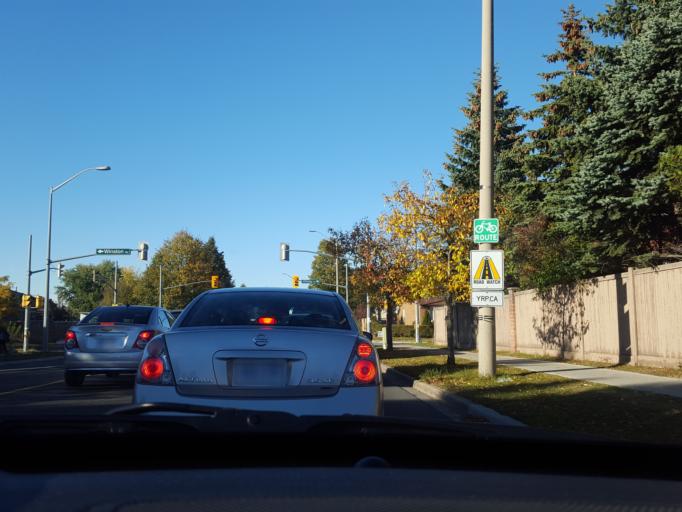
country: CA
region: Ontario
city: Markham
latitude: 43.8295
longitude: -79.2871
